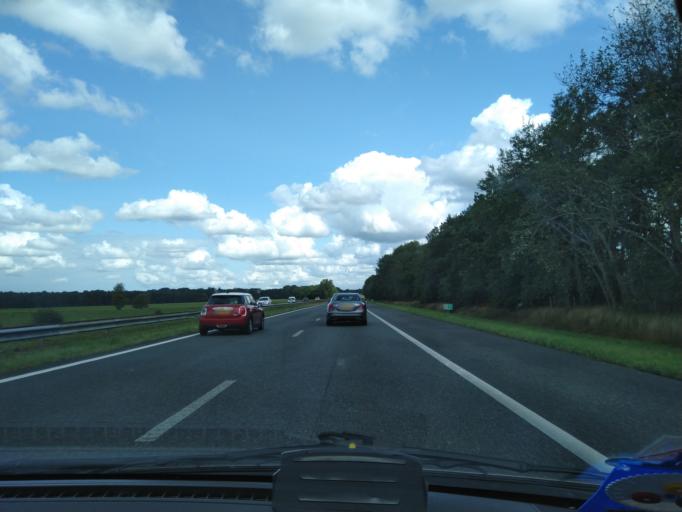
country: NL
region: Drenthe
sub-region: Gemeente Tynaarlo
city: Vries
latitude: 53.0514
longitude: 6.5935
